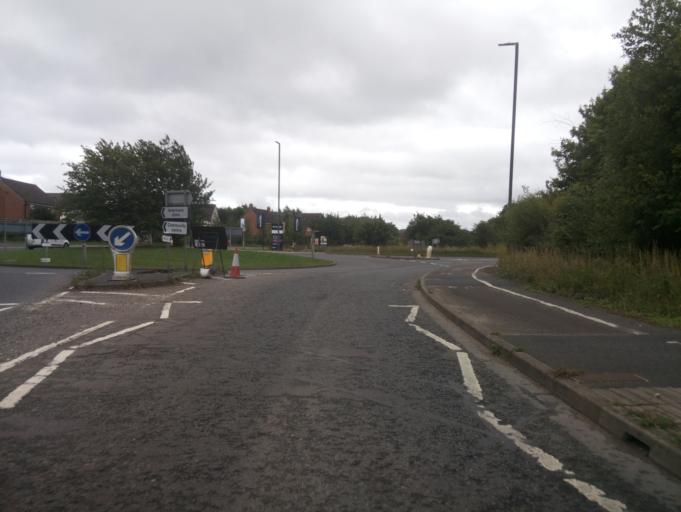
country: GB
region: England
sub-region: Gloucestershire
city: Tewkesbury
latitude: 51.9809
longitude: -2.1450
